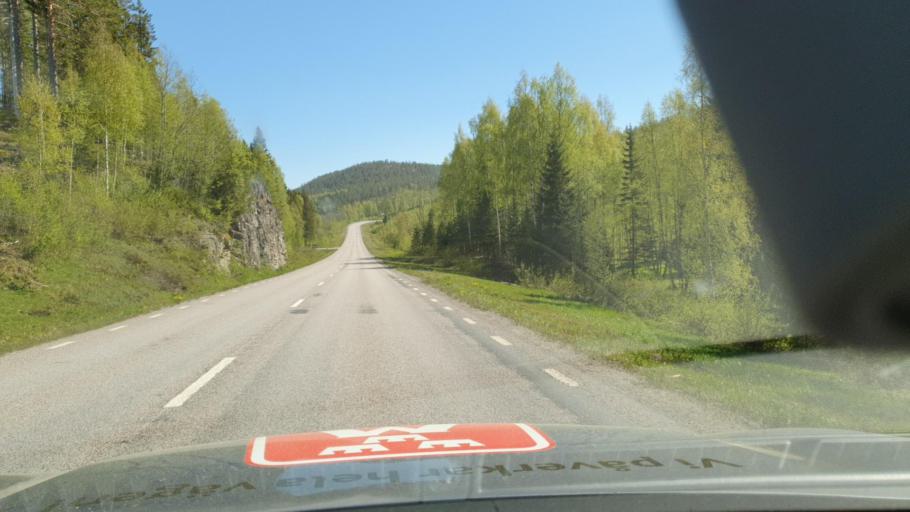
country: SE
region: Vaesternorrland
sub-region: OErnskoeldsviks Kommun
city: Ornskoldsvik
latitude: 63.3879
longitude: 18.6828
